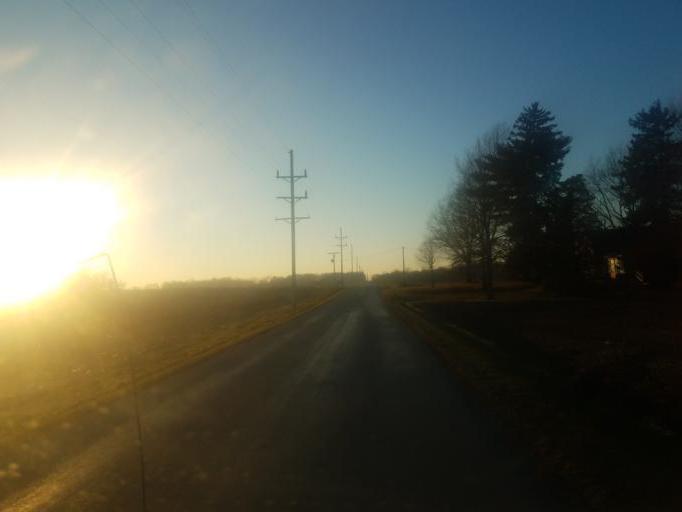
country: US
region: Ohio
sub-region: Wyandot County
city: Upper Sandusky
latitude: 40.8147
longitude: -83.1521
